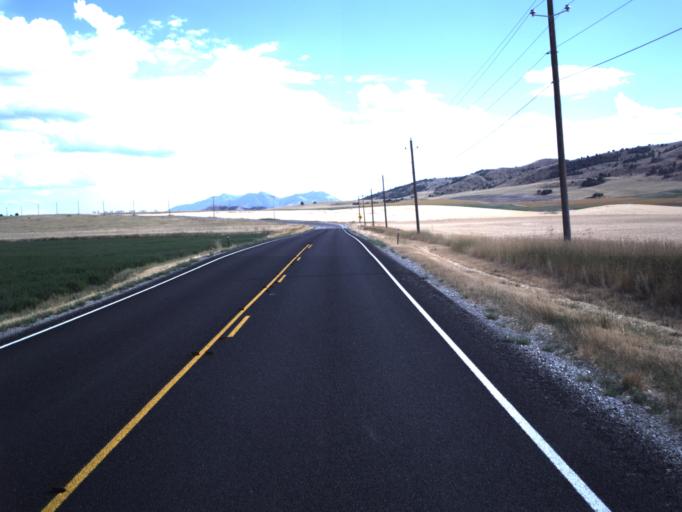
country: US
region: Utah
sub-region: Cache County
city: Benson
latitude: 41.9018
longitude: -112.0458
